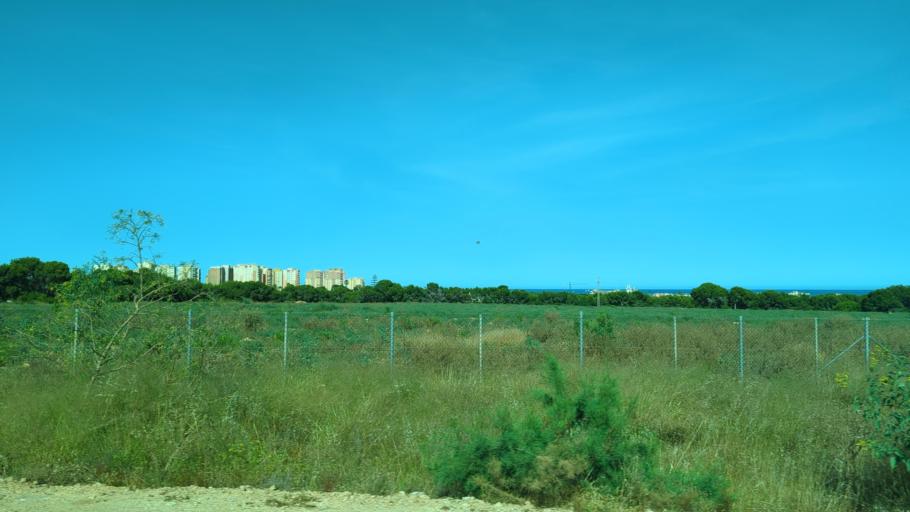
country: ES
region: Valencia
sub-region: Provincia de Alicante
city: Pilar de la Horadada
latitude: 37.8939
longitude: -0.7668
